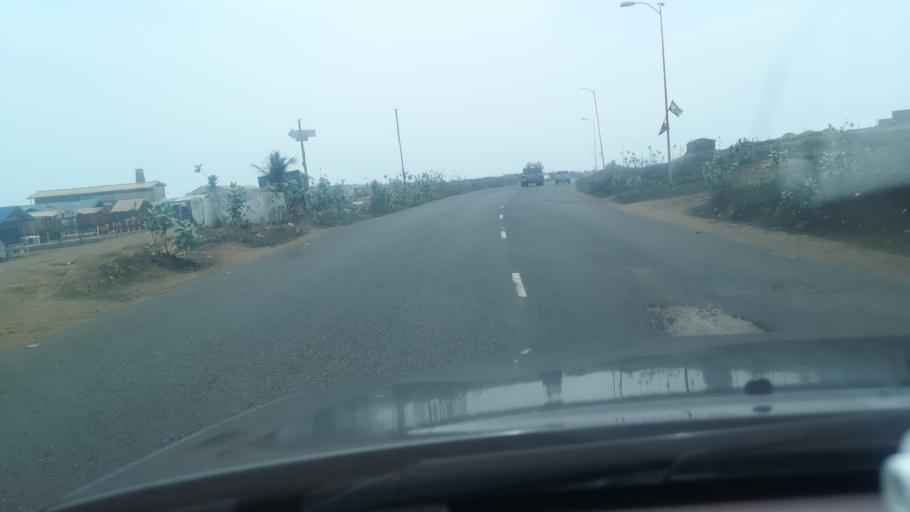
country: GH
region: Greater Accra
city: Nungua
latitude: 5.6104
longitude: -0.0496
